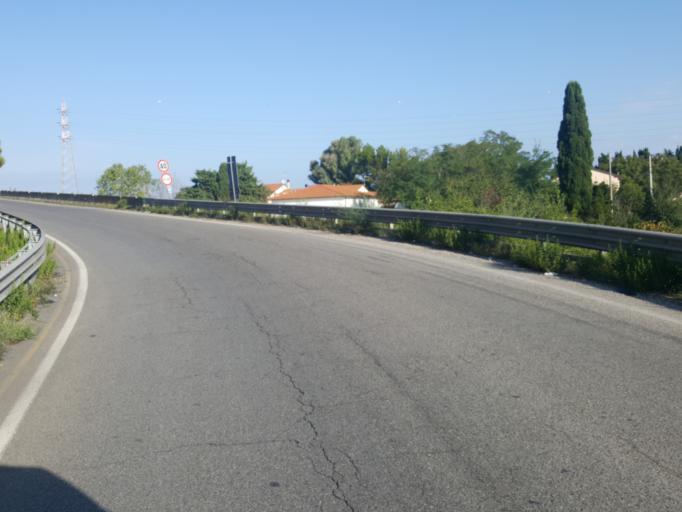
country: IT
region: Tuscany
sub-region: Provincia di Livorno
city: Livorno
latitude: 43.5322
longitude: 10.3358
